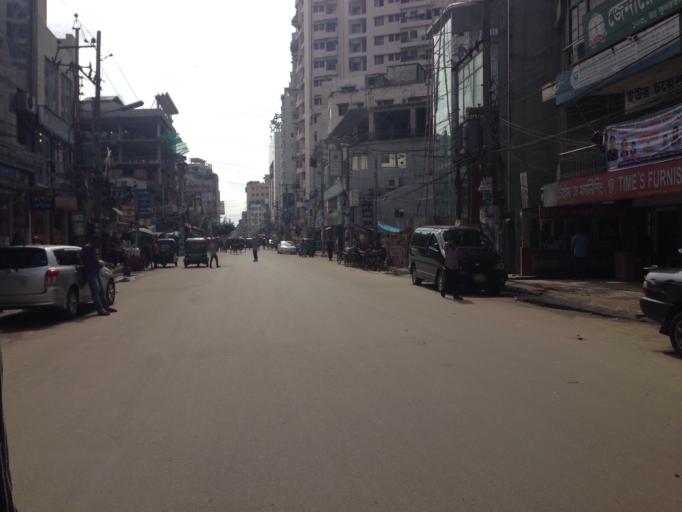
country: BD
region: Dhaka
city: Azimpur
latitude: 23.7384
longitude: 90.3879
